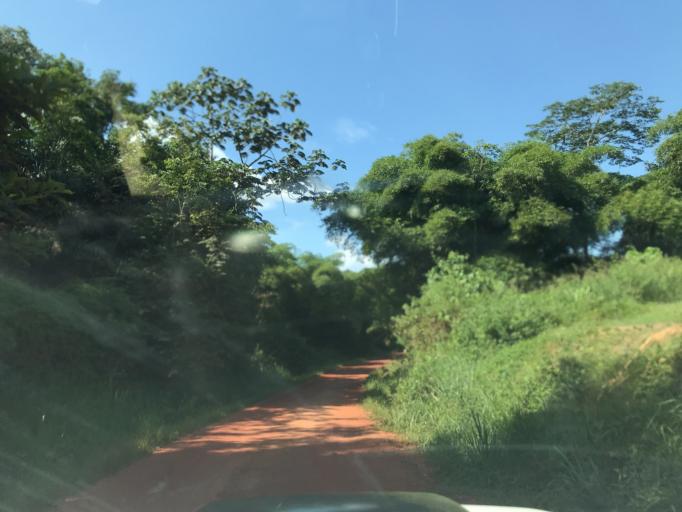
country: CD
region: Eastern Province
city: Kisangani
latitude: 1.2045
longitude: 25.2588
